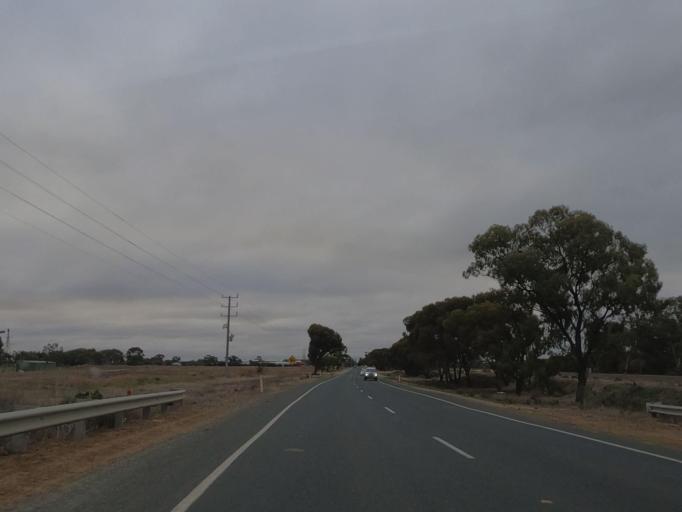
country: AU
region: Victoria
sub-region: Swan Hill
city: Swan Hill
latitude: -35.3948
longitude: 143.5724
